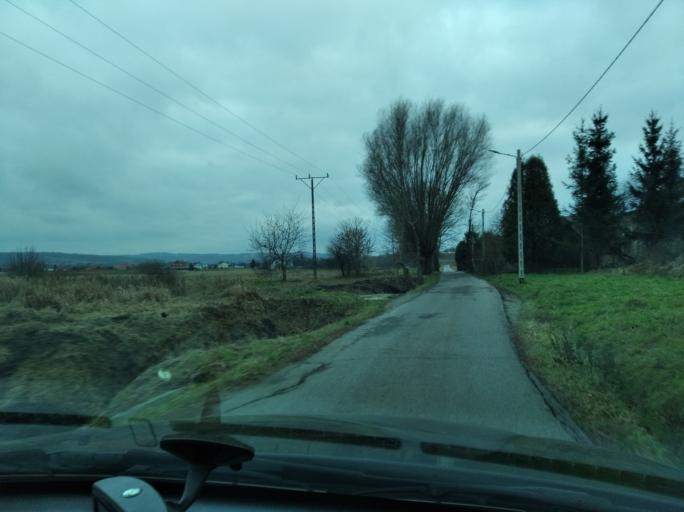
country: PL
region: Subcarpathian Voivodeship
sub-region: Powiat rzeszowski
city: Lutoryz
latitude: 49.9726
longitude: 21.9257
